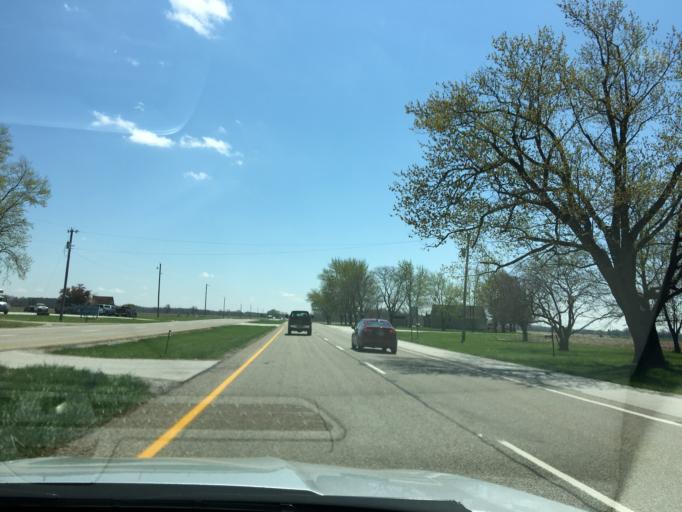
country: US
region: Indiana
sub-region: Boone County
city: Thorntown
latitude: 40.1711
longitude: -86.6099
